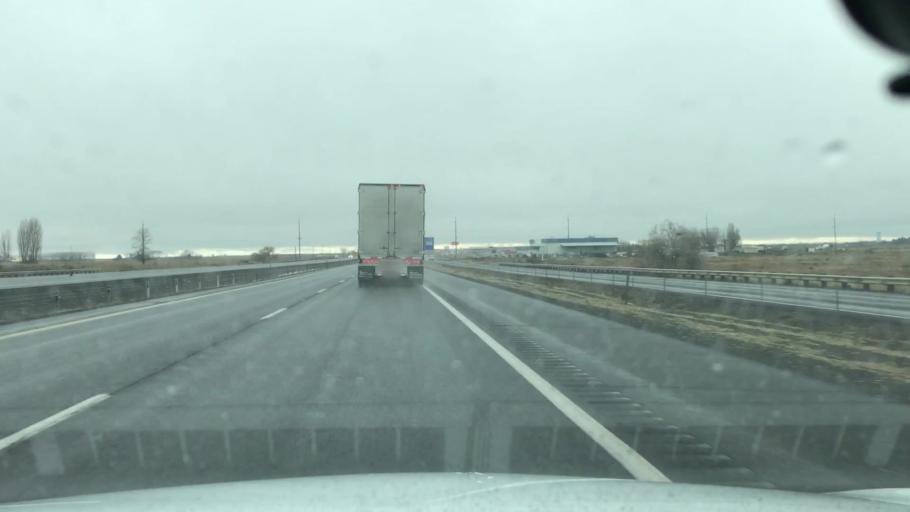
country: US
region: Washington
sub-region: Grant County
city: Moses Lake
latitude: 47.0943
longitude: -119.2060
